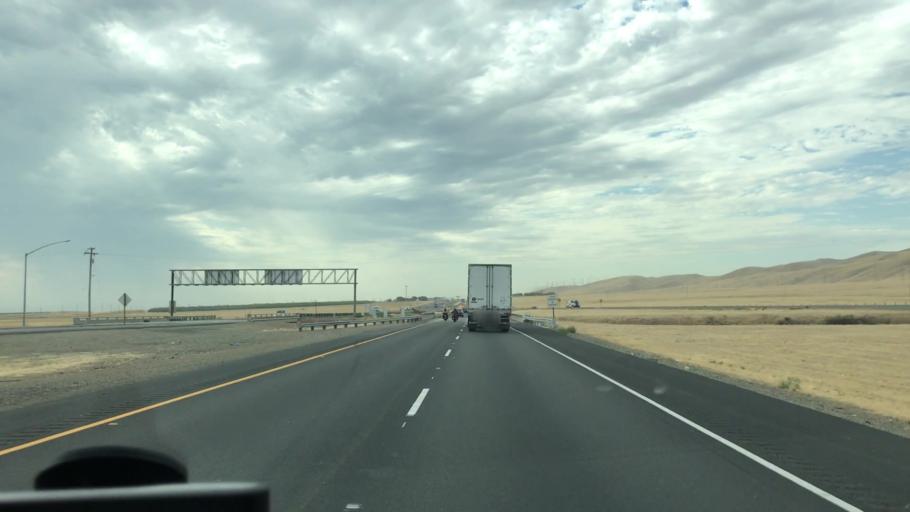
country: US
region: California
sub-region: San Joaquin County
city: Tracy
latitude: 37.5947
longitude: -121.3388
